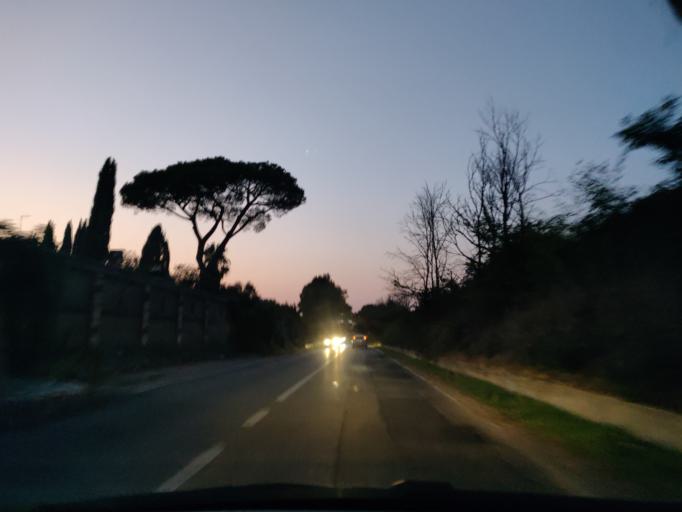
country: IT
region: Latium
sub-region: Citta metropolitana di Roma Capitale
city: Npp 23 (Parco Leonardo)
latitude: 41.8453
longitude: 12.2707
